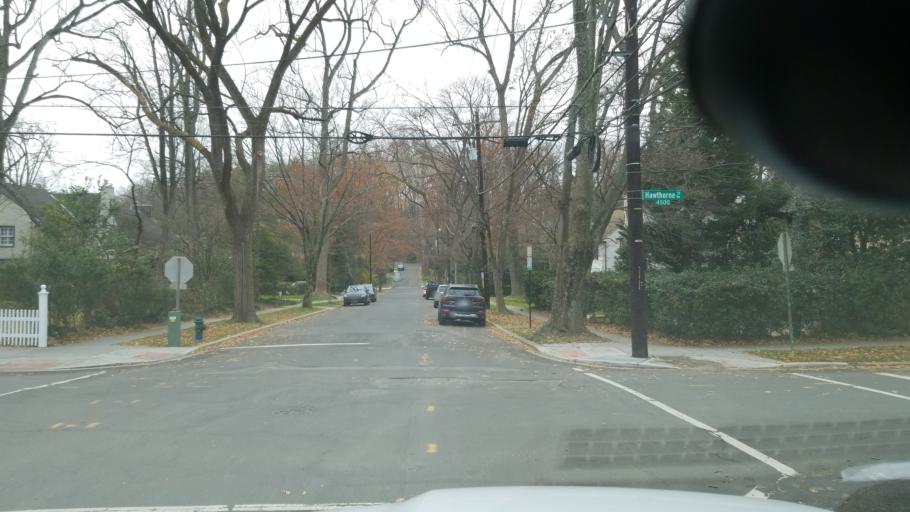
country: US
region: Maryland
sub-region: Montgomery County
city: Friendship Village
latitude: 38.9290
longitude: -77.0886
